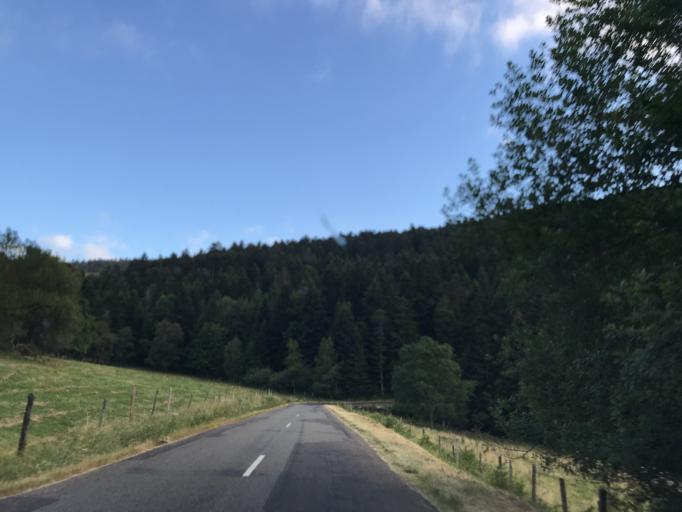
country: FR
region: Rhone-Alpes
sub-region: Departement de la Loire
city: Noiretable
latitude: 45.7550
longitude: 3.8269
